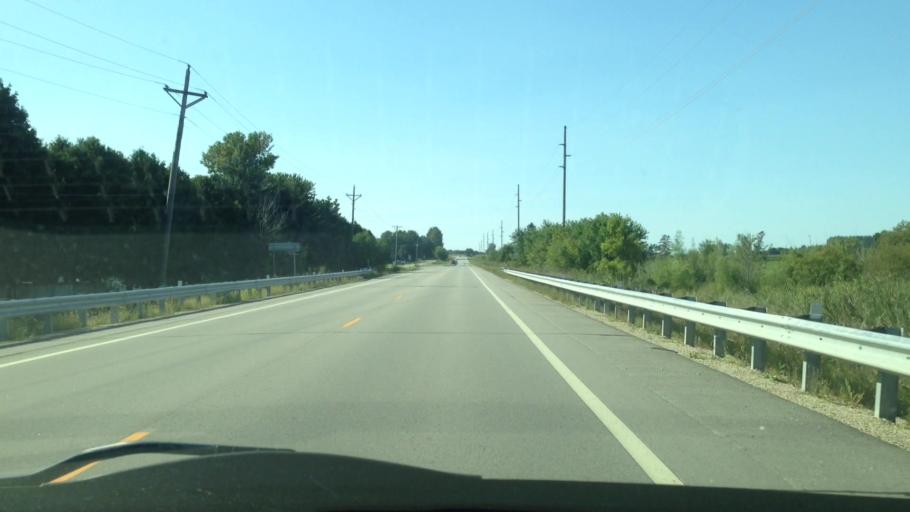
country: US
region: Minnesota
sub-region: Olmsted County
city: Eyota
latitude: 43.9919
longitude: -92.2303
